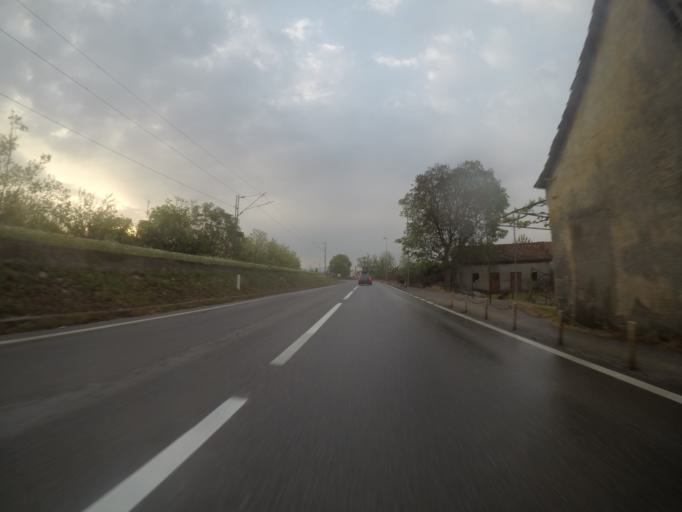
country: ME
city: Mojanovici
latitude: 42.3042
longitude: 19.1903
